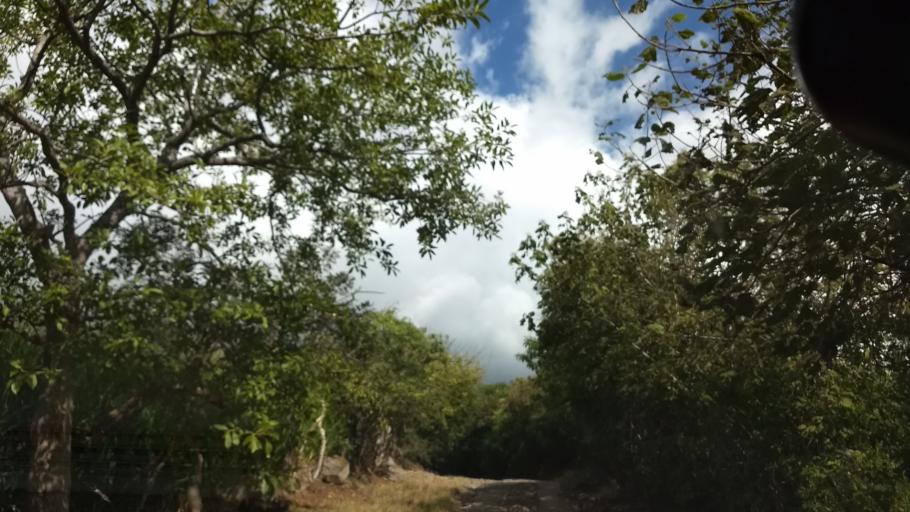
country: MX
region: Colima
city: Suchitlan
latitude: 19.4560
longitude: -103.7692
